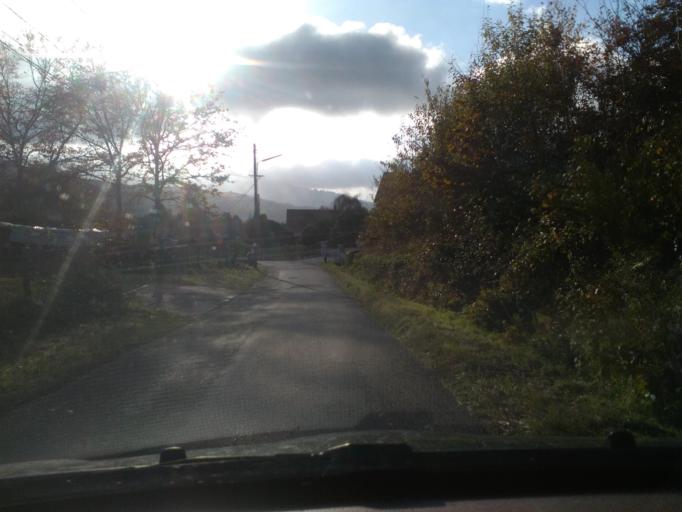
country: FR
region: Lorraine
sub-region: Departement des Vosges
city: Fraize
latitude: 48.1932
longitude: 7.0074
